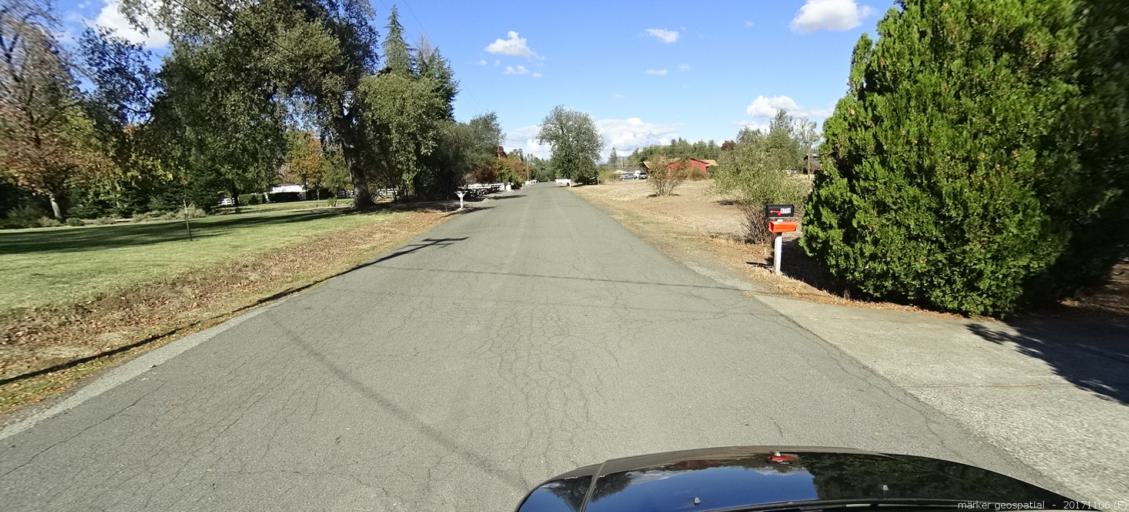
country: US
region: California
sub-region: Shasta County
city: Palo Cedro
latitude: 40.5711
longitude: -122.2236
